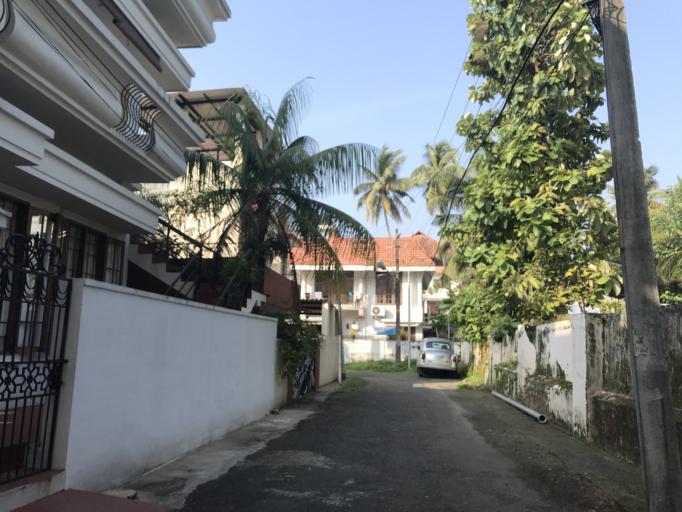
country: IN
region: Kerala
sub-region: Ernakulam
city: Cochin
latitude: 9.9663
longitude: 76.2448
